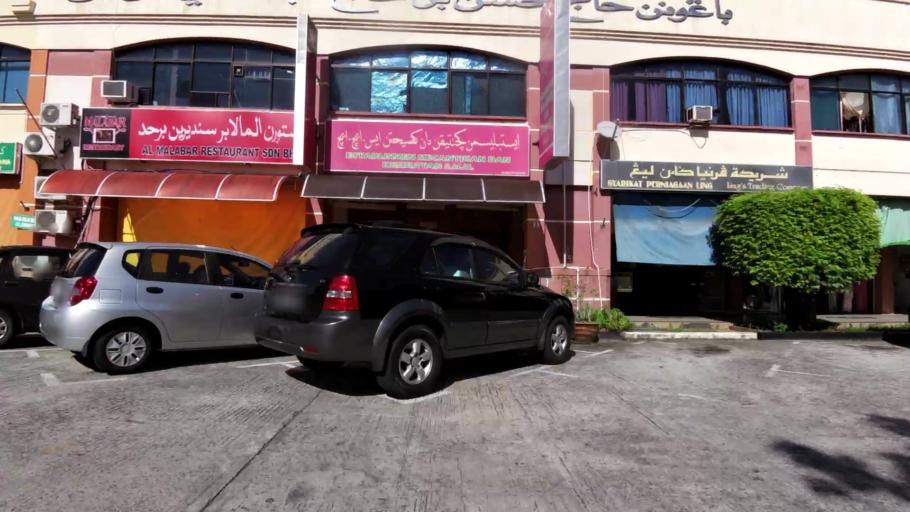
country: BN
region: Belait
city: Kuala Belait
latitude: 4.5847
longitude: 114.2139
